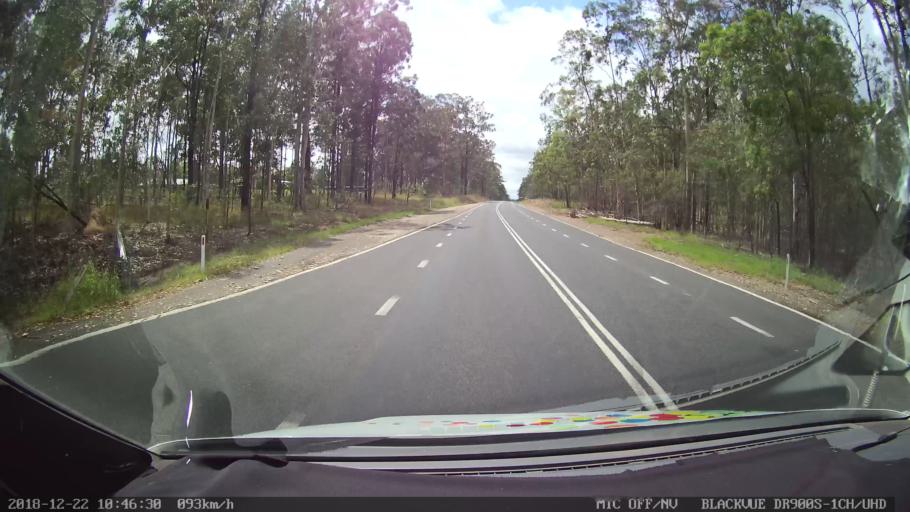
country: AU
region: New South Wales
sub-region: Clarence Valley
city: South Grafton
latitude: -29.6663
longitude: 152.8263
